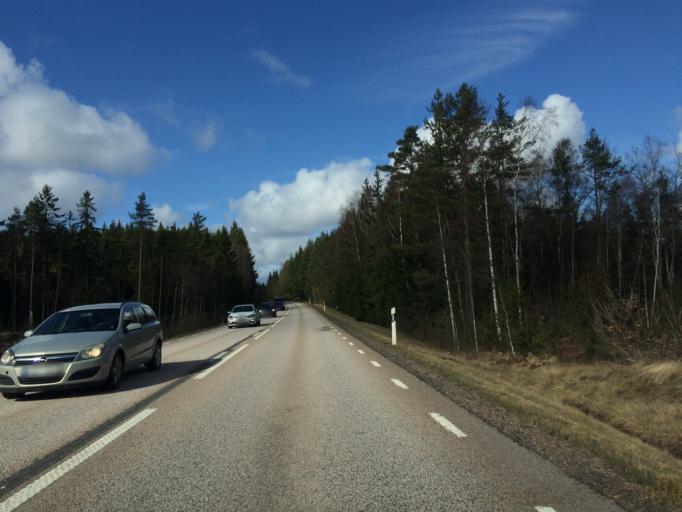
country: SE
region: Kronoberg
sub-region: Markaryds Kommun
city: Markaryd
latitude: 56.4841
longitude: 13.4807
